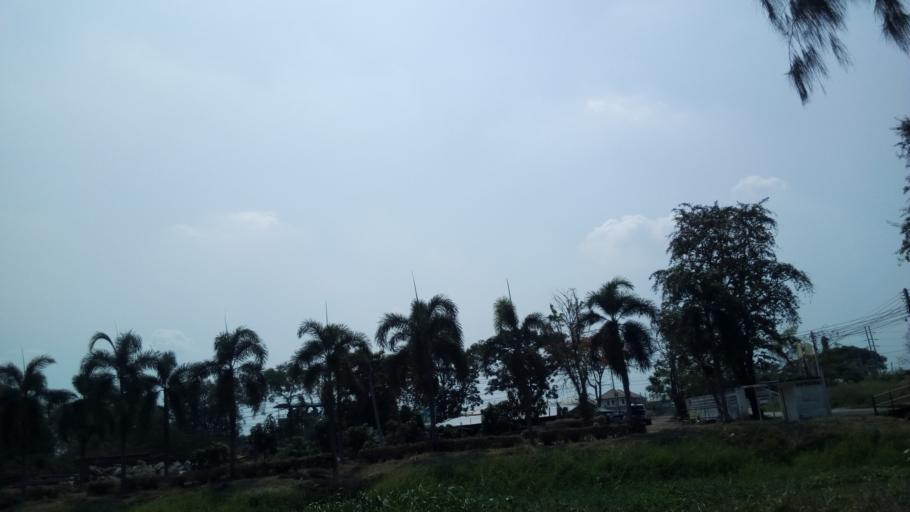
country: TH
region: Sara Buri
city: Nong Khae
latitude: 14.3307
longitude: 100.8744
